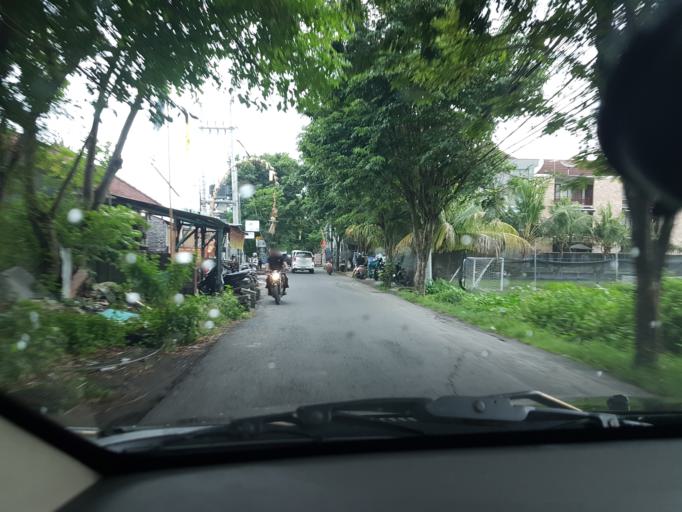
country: ID
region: Bali
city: Kuta
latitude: -8.6796
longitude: 115.1629
